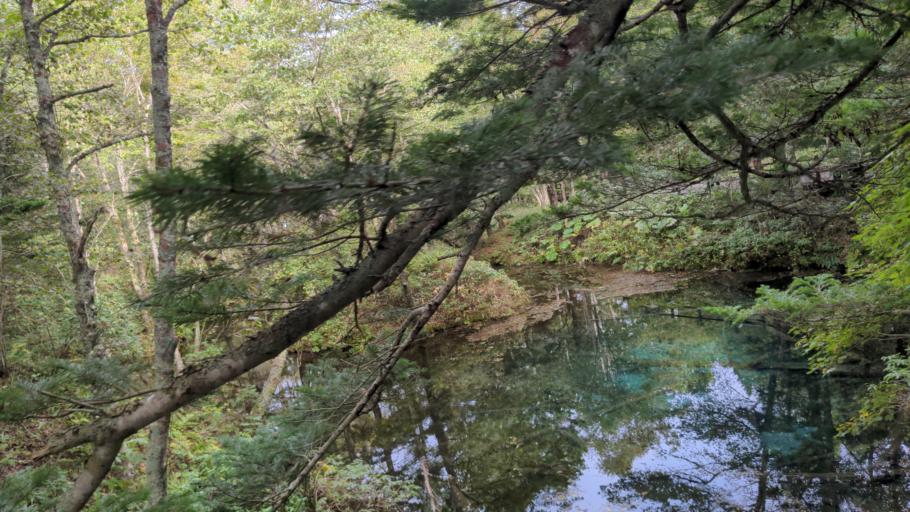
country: JP
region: Hokkaido
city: Abashiri
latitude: 43.6449
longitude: 144.5500
